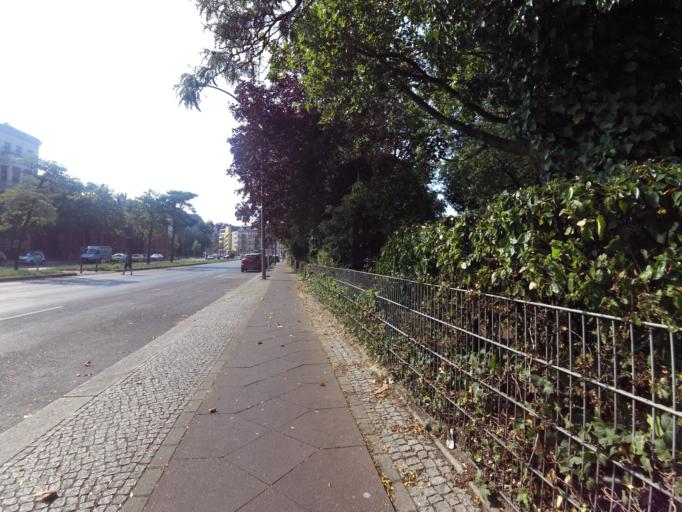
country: DE
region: Berlin
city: Friedenau
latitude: 52.4725
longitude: 13.3286
